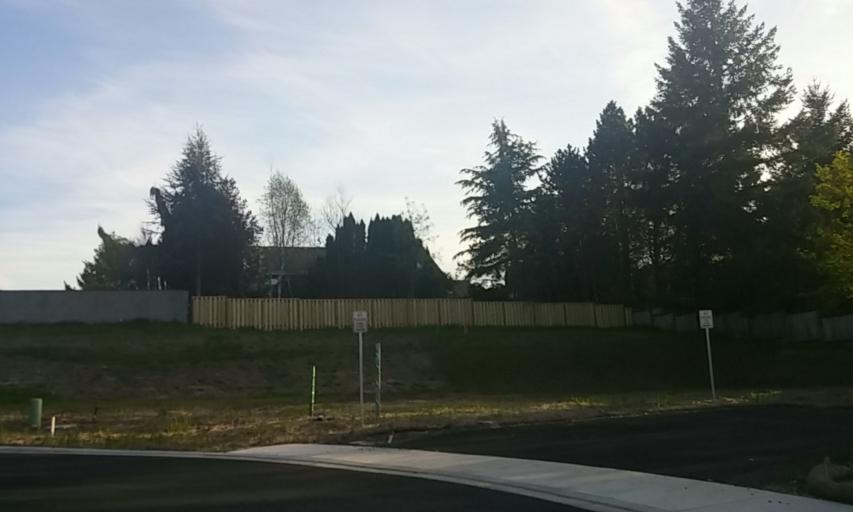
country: US
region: Oregon
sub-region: Washington County
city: Cedar Mill
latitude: 45.5409
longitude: -122.7938
